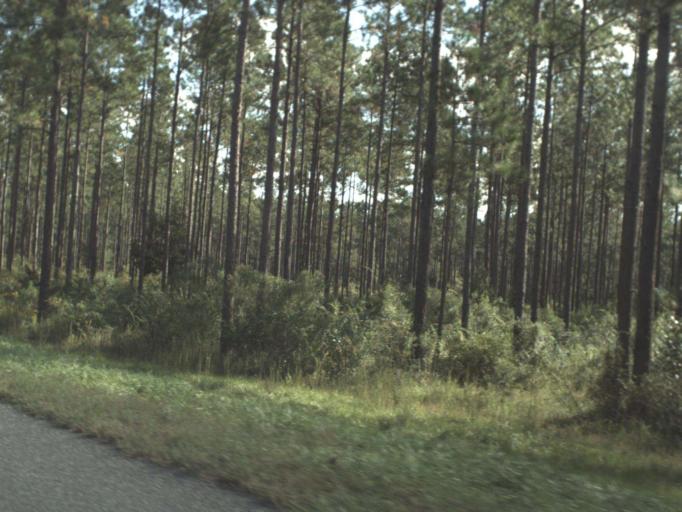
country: US
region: Florida
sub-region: Calhoun County
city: Blountstown
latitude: 30.3453
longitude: -85.1148
